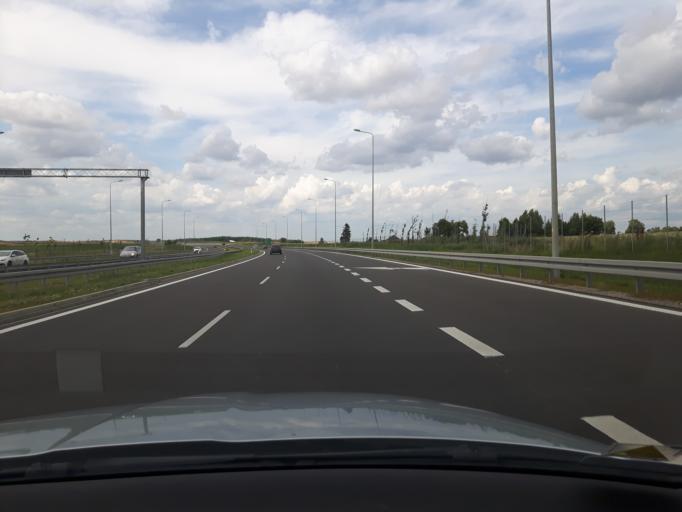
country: PL
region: Warmian-Masurian Voivodeship
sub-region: Powiat nidzicki
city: Nidzica
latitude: 53.3336
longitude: 20.4361
